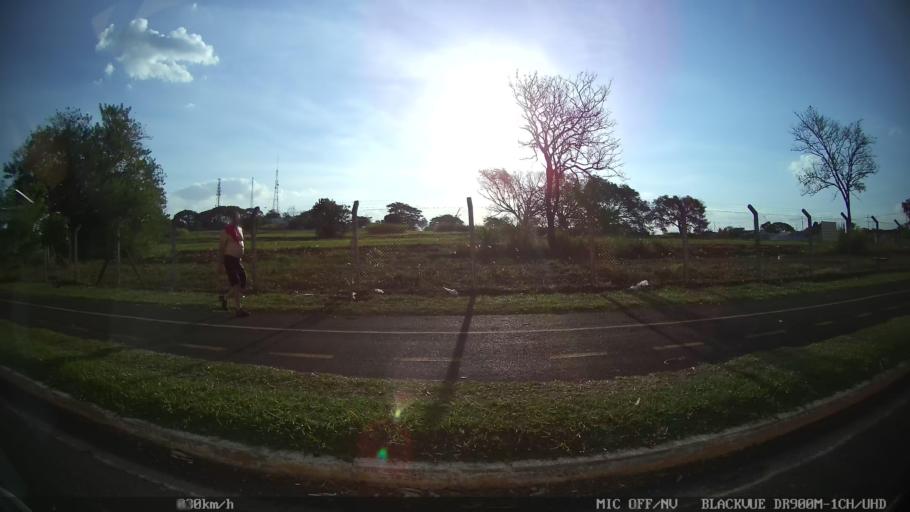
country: BR
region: Sao Paulo
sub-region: Ribeirao Preto
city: Ribeirao Preto
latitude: -21.1619
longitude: -47.8425
